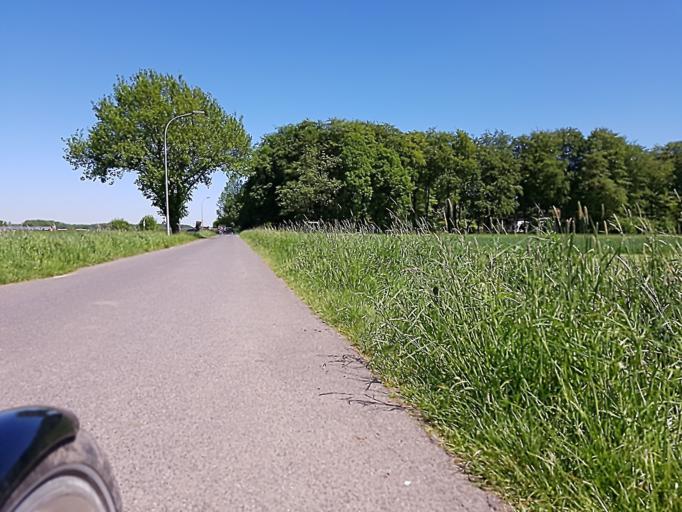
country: DE
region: North Rhine-Westphalia
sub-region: Regierungsbezirk Dusseldorf
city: Grefrath
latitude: 51.3309
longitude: 6.3528
